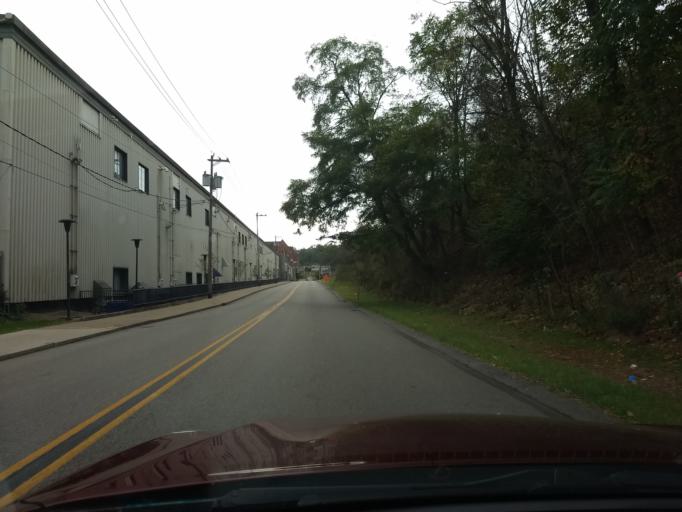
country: US
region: Pennsylvania
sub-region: Allegheny County
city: Turtle Creek
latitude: 40.4021
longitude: -79.8321
